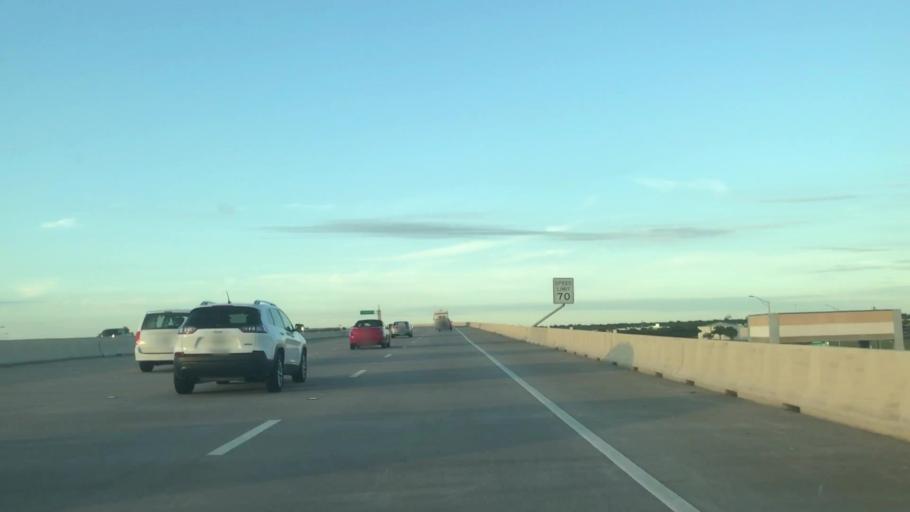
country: US
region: Texas
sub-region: Dallas County
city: Farmers Branch
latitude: 32.9473
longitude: -96.9270
